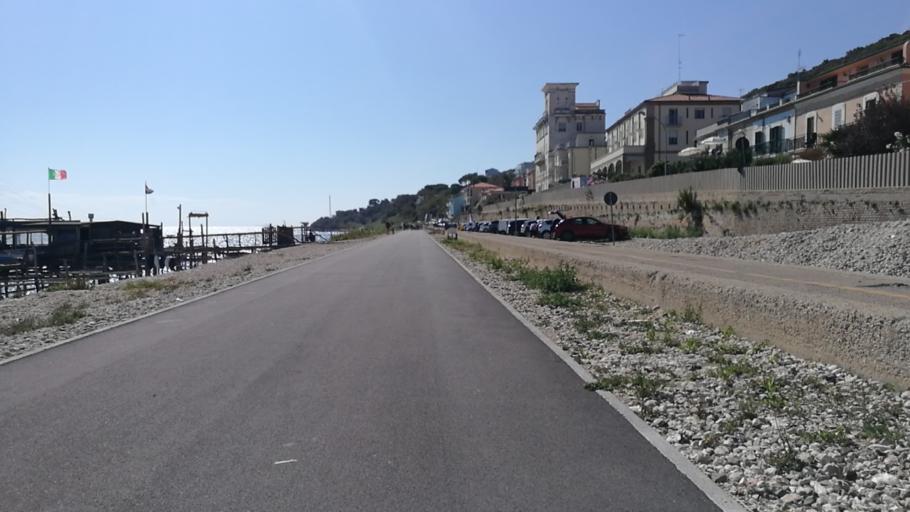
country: IT
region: Abruzzo
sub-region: Provincia di Chieti
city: Marina di San Vito
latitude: 42.3061
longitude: 14.4500
